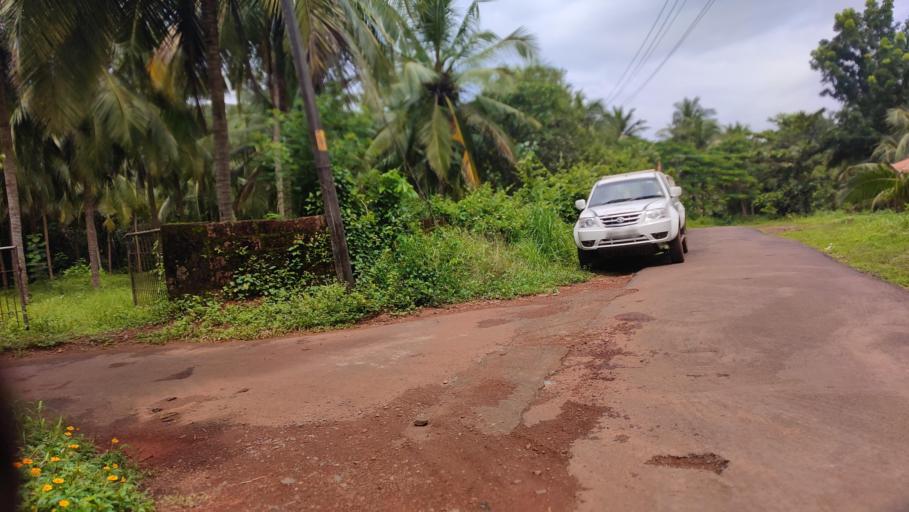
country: IN
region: Kerala
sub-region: Kasaragod District
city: Kannangad
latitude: 12.4012
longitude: 75.0550
